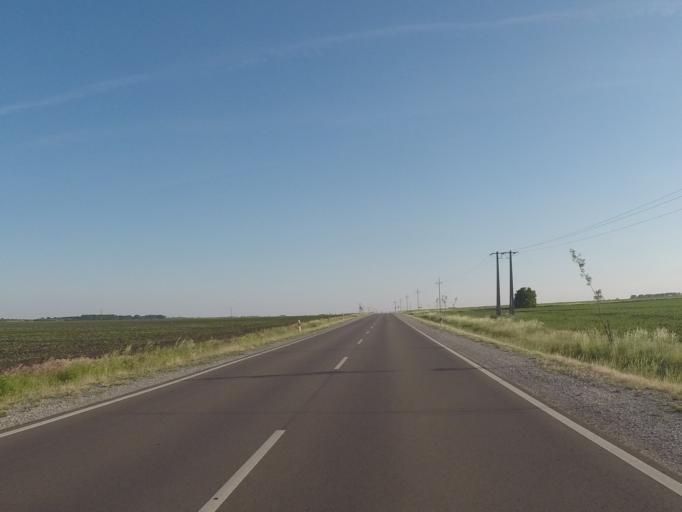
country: HU
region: Heves
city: Besenyotelek
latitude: 47.7100
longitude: 20.4095
